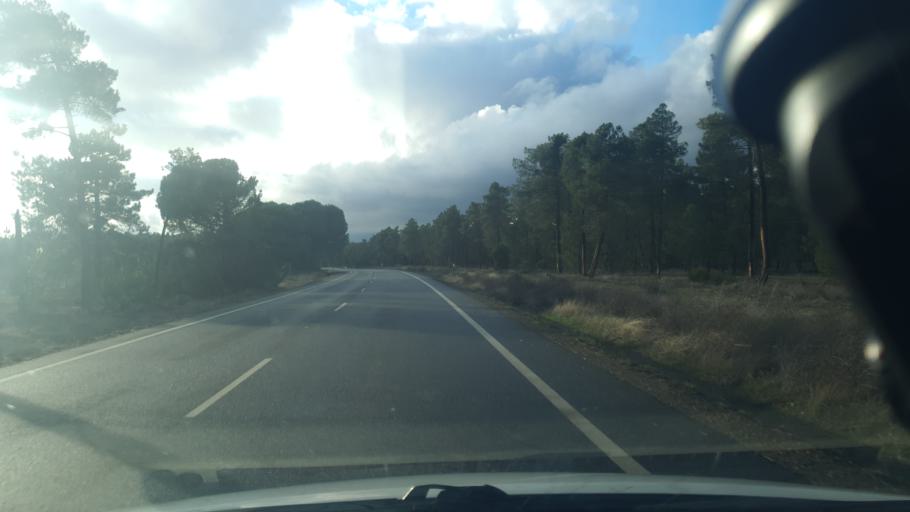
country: ES
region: Castille and Leon
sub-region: Provincia de Segovia
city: Nava de la Asuncion
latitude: 41.1557
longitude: -4.5206
